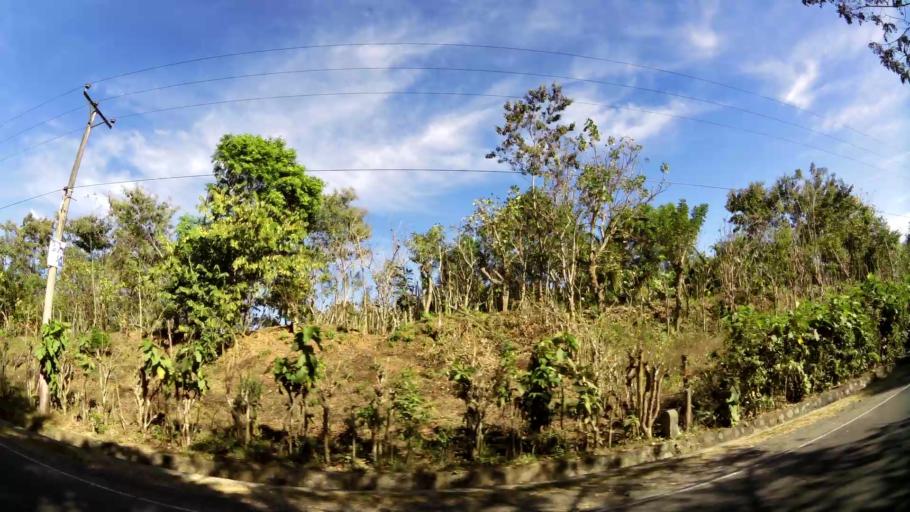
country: SV
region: Cuscatlan
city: Tenancingo
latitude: 13.8389
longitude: -89.0282
